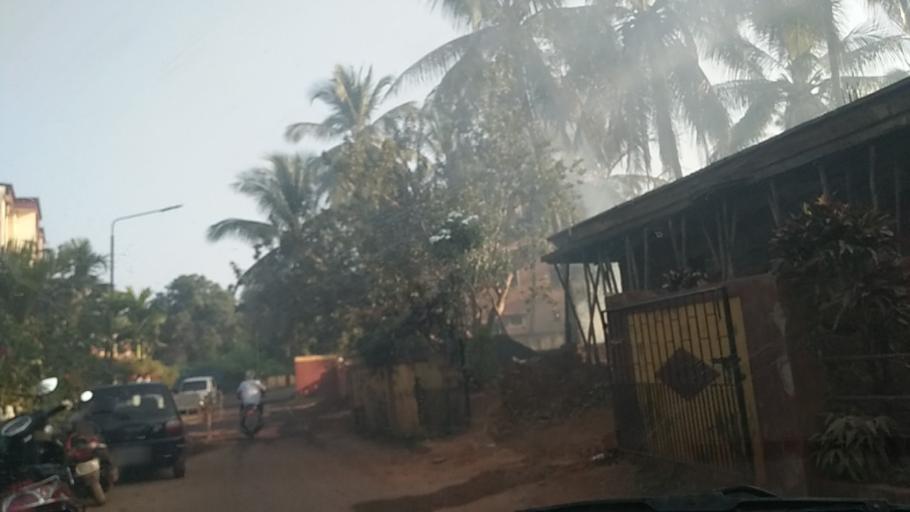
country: IN
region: Goa
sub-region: South Goa
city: Madgaon
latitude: 15.2753
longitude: 73.9532
